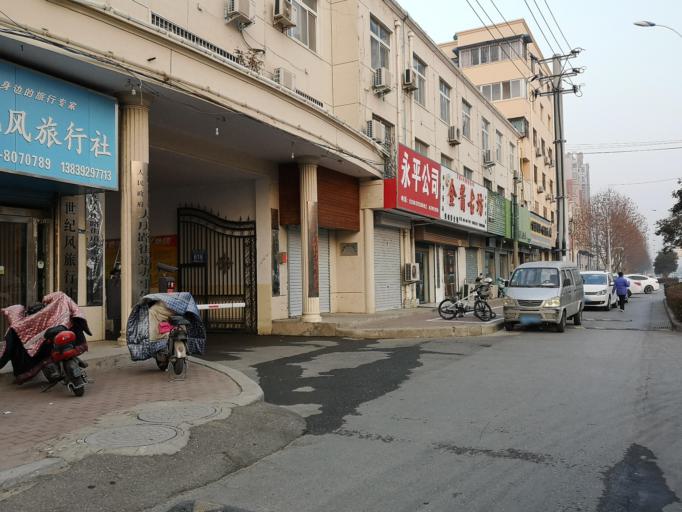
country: CN
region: Henan Sheng
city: Zhongyuanlu
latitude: 35.7582
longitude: 115.0725
